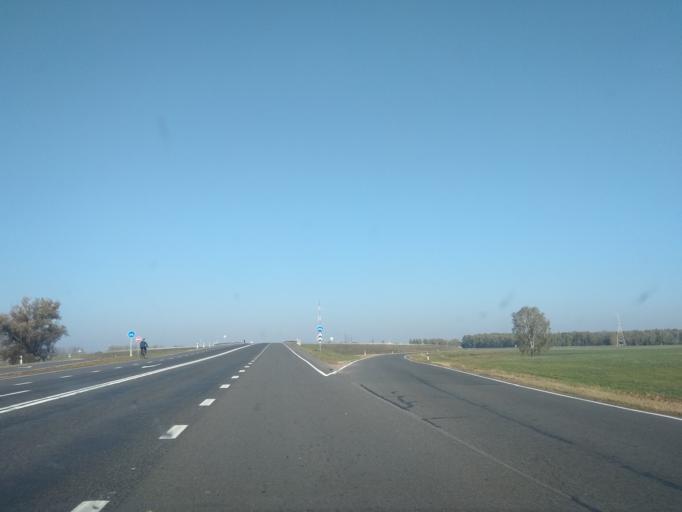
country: BY
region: Brest
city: Kobryn
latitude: 52.1777
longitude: 24.3256
